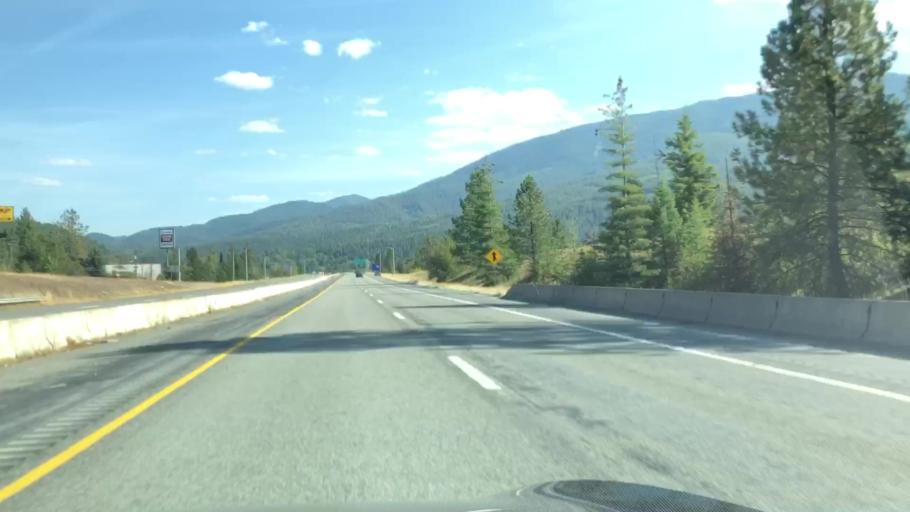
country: US
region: Idaho
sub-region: Shoshone County
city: Kellogg
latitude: 47.5454
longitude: -116.1325
